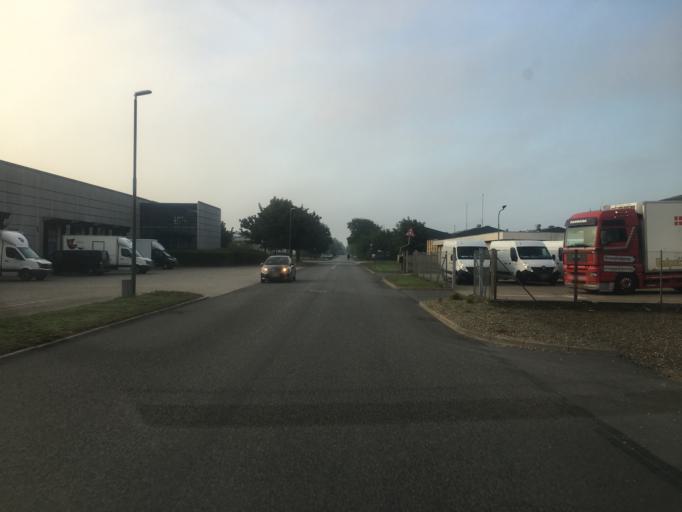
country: DK
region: South Denmark
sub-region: Tonder Kommune
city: Tonder
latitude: 54.9558
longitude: 8.8677
